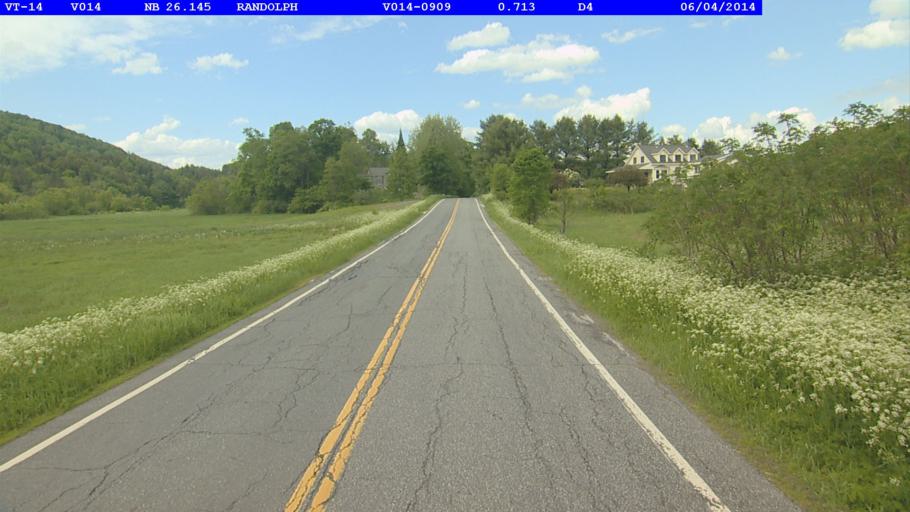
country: US
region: Vermont
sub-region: Orange County
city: Randolph
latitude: 43.8861
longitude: -72.5812
